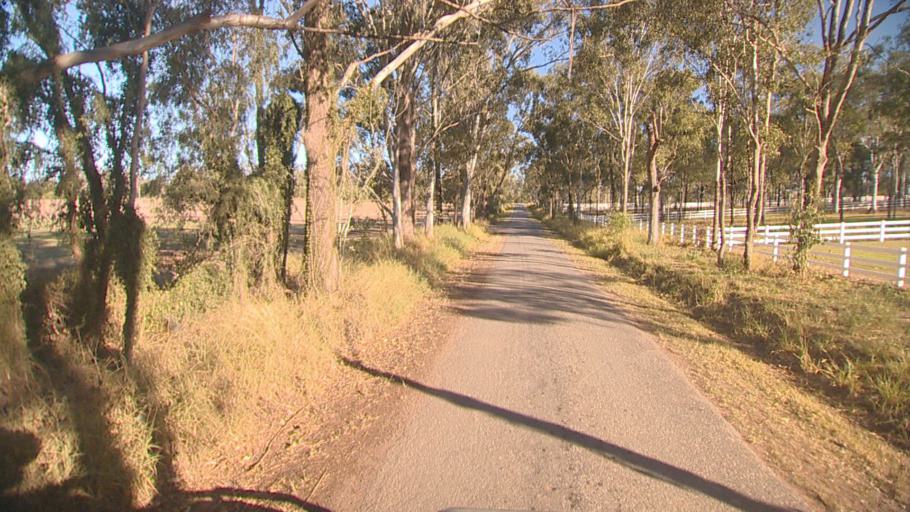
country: AU
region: Queensland
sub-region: Logan
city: North Maclean
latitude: -27.7754
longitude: 153.0380
